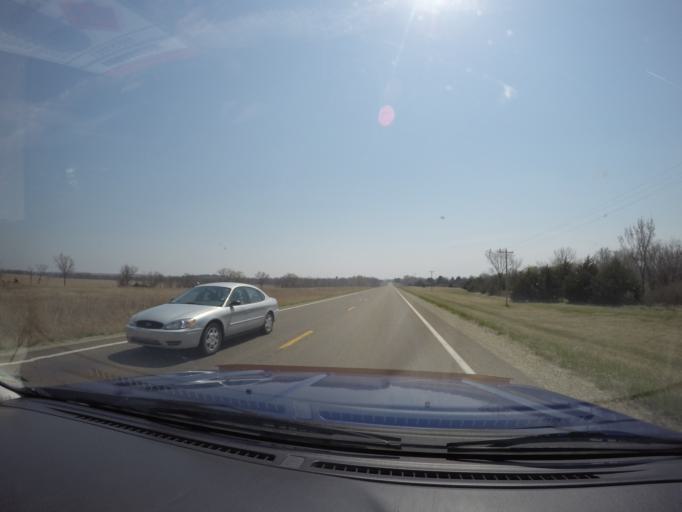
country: US
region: Kansas
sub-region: Morris County
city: Council Grove
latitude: 38.7099
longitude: -96.4974
